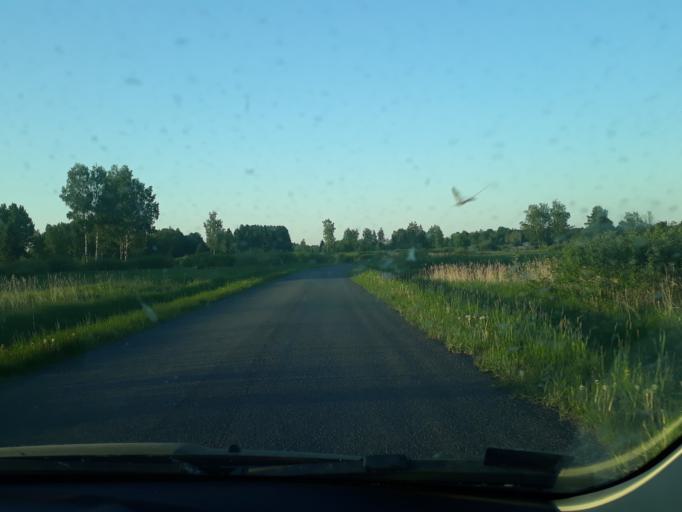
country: EE
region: Paernumaa
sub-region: Vaendra vald (alev)
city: Vandra
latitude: 58.5683
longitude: 24.9835
